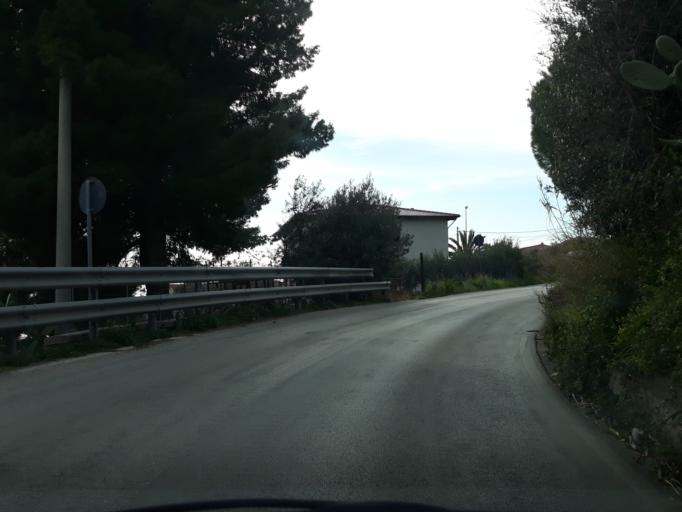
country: IT
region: Sicily
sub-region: Palermo
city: Montelepre
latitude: 38.0880
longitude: 13.1663
